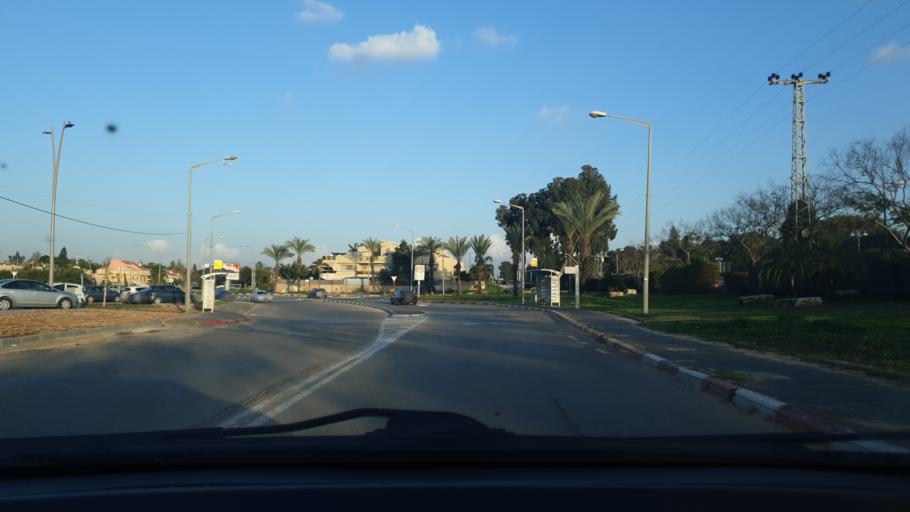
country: IL
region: Central District
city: Ness Ziona
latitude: 31.9331
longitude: 34.8289
